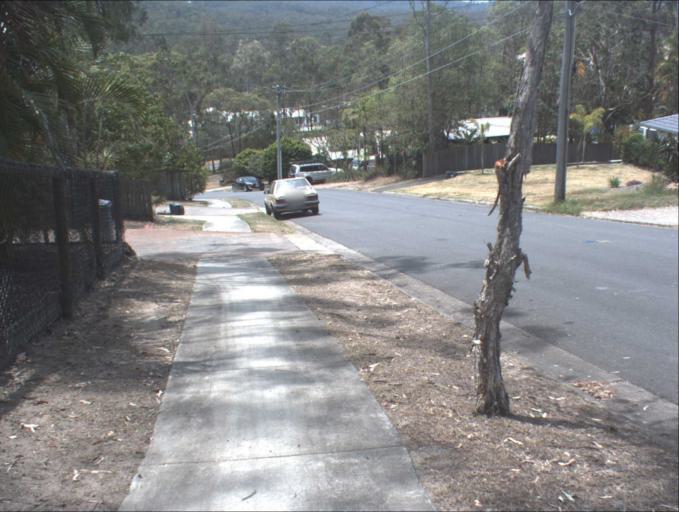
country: AU
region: Queensland
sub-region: Logan
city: Slacks Creek
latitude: -27.6607
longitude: 153.1977
